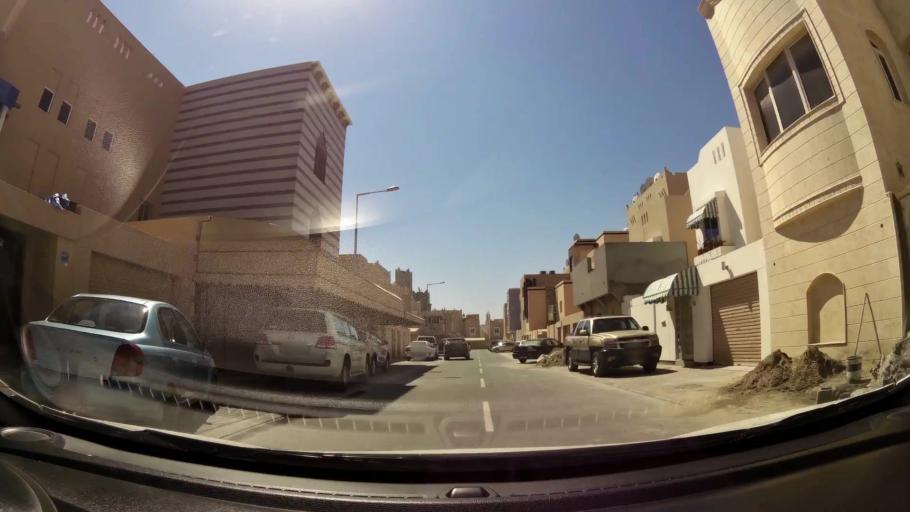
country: BH
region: Muharraq
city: Al Muharraq
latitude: 26.2746
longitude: 50.5966
